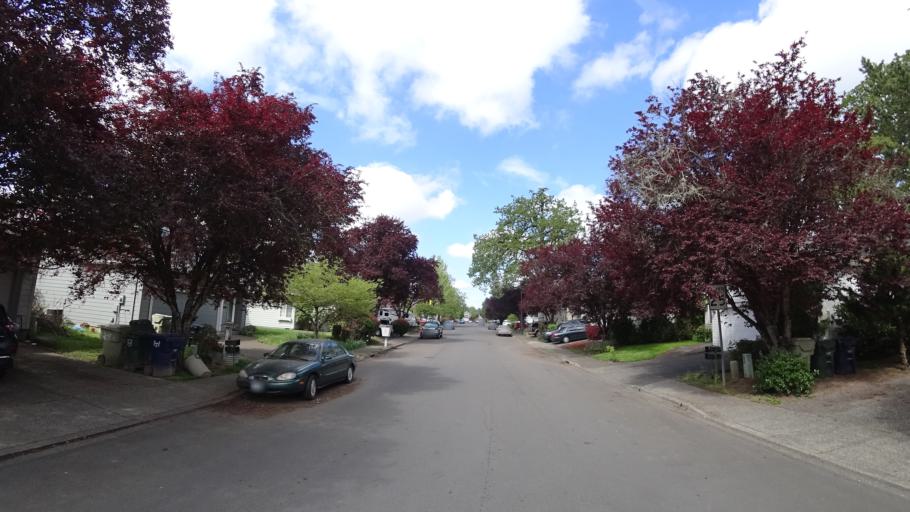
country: US
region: Oregon
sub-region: Washington County
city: Aloha
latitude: 45.5128
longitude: -122.8840
